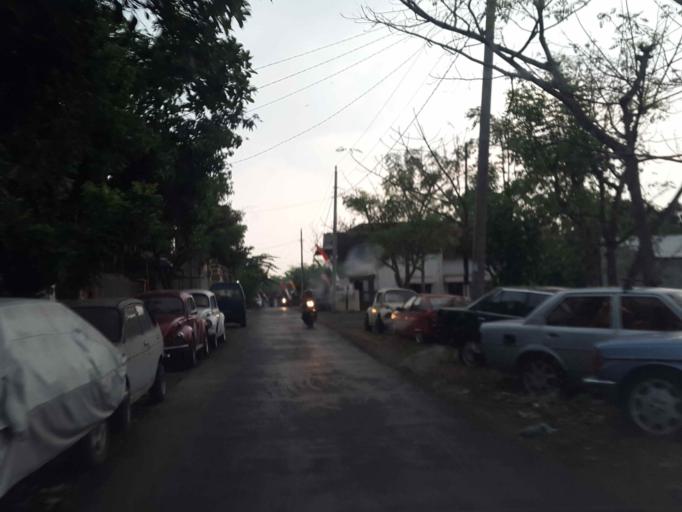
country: ID
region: Central Java
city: Surakarta
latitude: -7.5623
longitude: 110.8647
